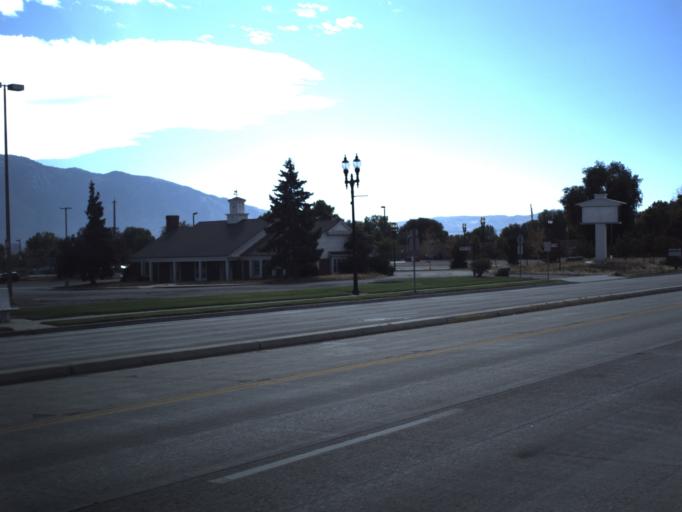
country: US
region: Utah
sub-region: Salt Lake County
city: West Jordan
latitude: 40.6067
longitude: -111.9389
